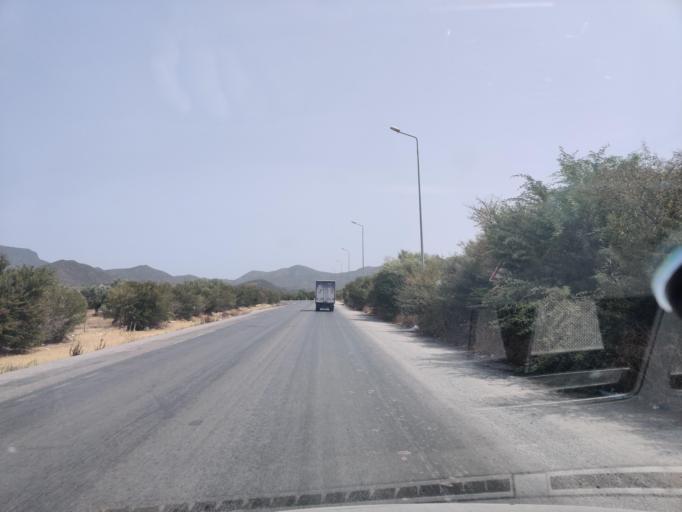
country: TN
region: Tunis
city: La Sebala du Mornag
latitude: 36.6644
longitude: 10.3236
